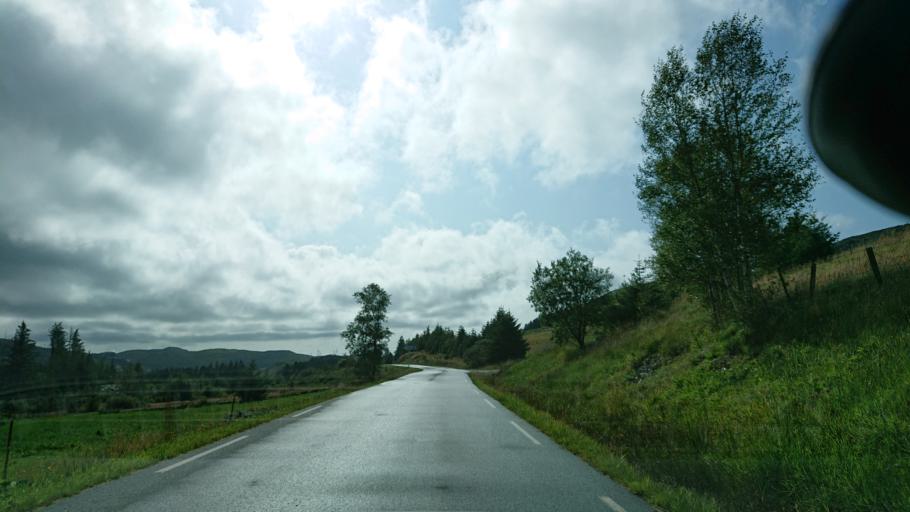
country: NO
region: Rogaland
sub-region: Gjesdal
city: Algard
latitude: 58.6856
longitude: 5.8693
